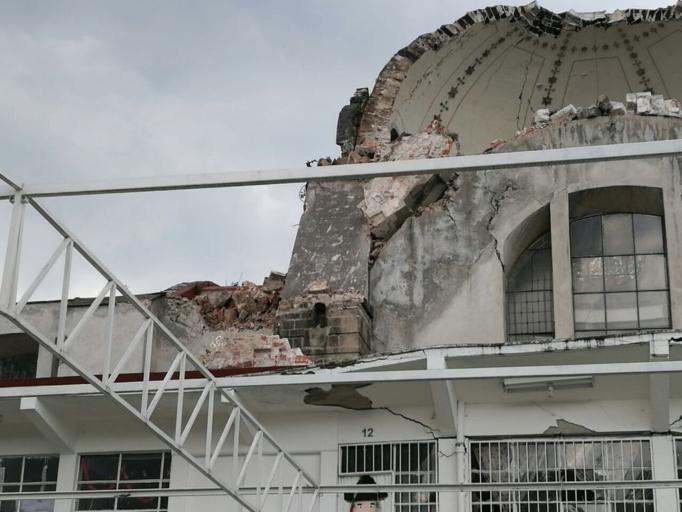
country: MX
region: Mexico City
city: Cuauhtemoc
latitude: 19.4490
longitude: -99.1420
